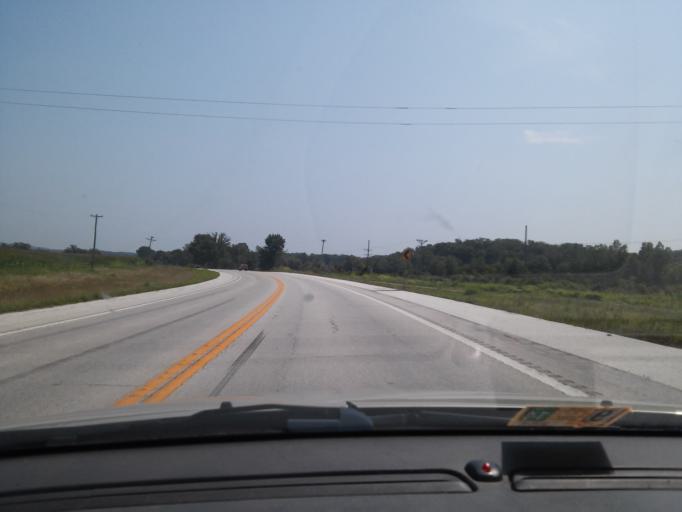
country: US
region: Missouri
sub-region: Pike County
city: Bowling Green
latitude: 39.3788
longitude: -91.1449
